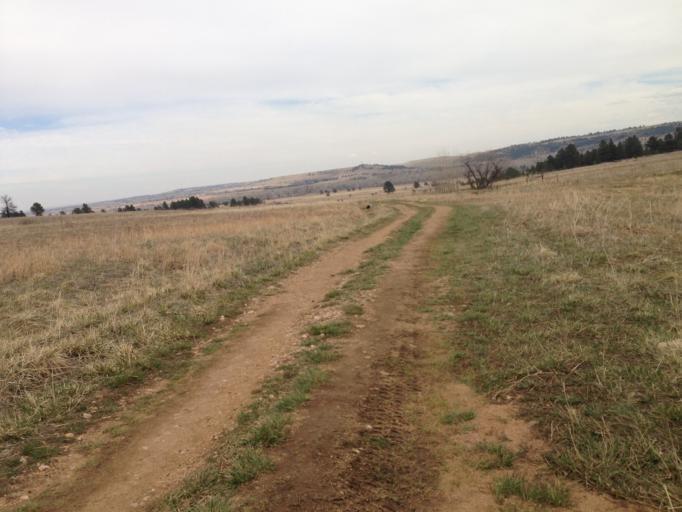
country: US
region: Colorado
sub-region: Boulder County
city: Boulder
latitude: 39.9550
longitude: -105.2630
